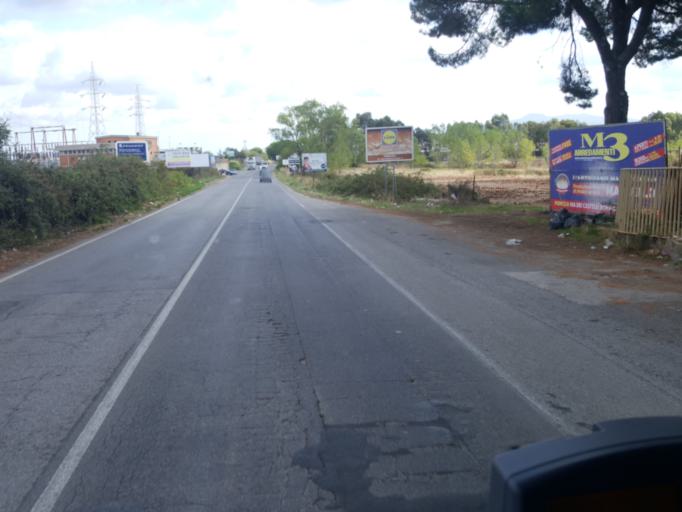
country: IT
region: Latium
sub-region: Citta metropolitana di Roma Capitale
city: Area Produttiva
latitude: 41.6890
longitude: 12.5157
